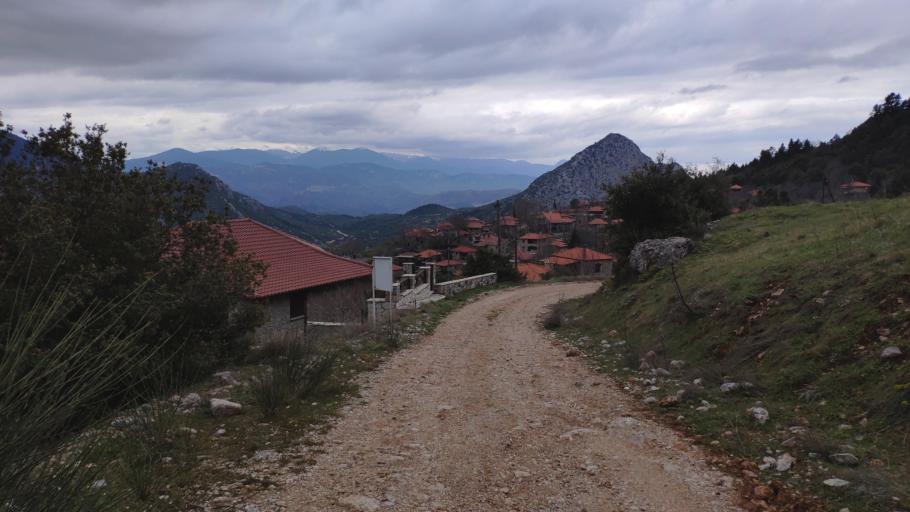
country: GR
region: Central Greece
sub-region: Nomos Fokidos
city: Amfissa
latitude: 38.6392
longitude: 22.4255
